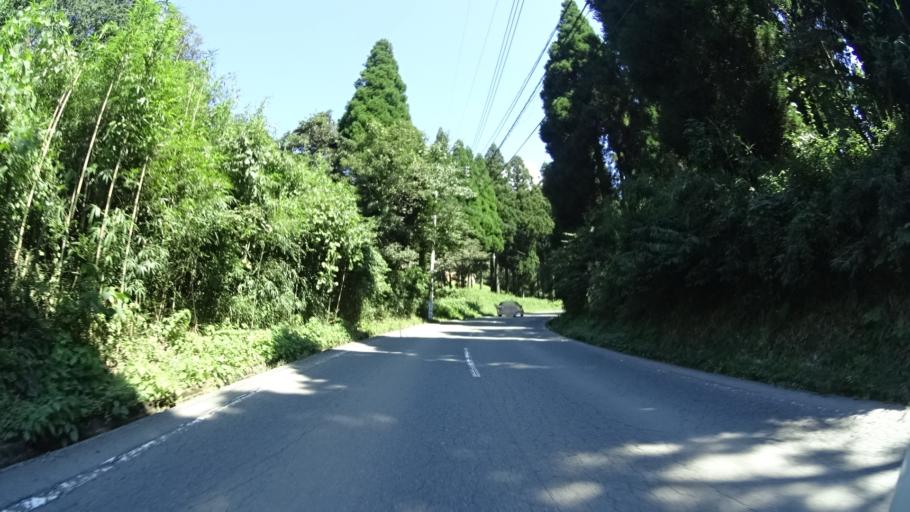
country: JP
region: Kumamoto
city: Aso
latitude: 32.8833
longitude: 131.0001
